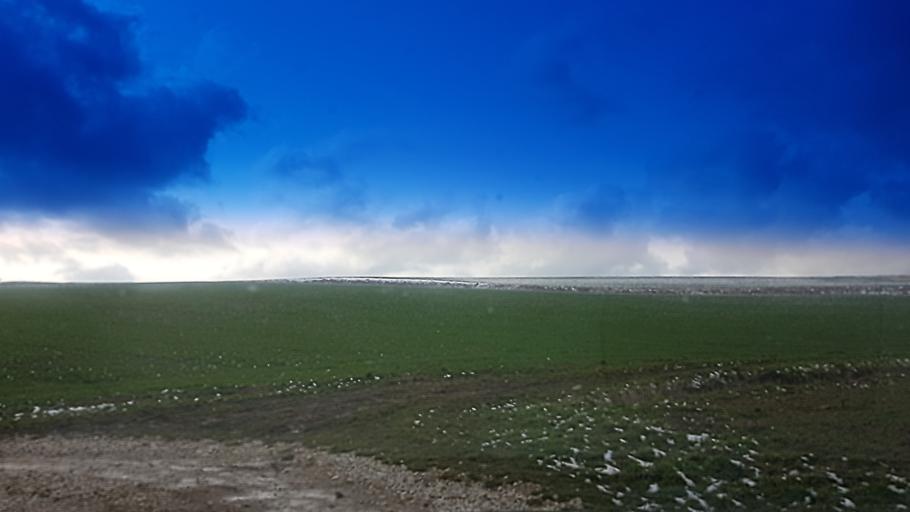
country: DE
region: Bavaria
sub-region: Upper Franconia
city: Schesslitz
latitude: 50.0056
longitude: 10.9987
